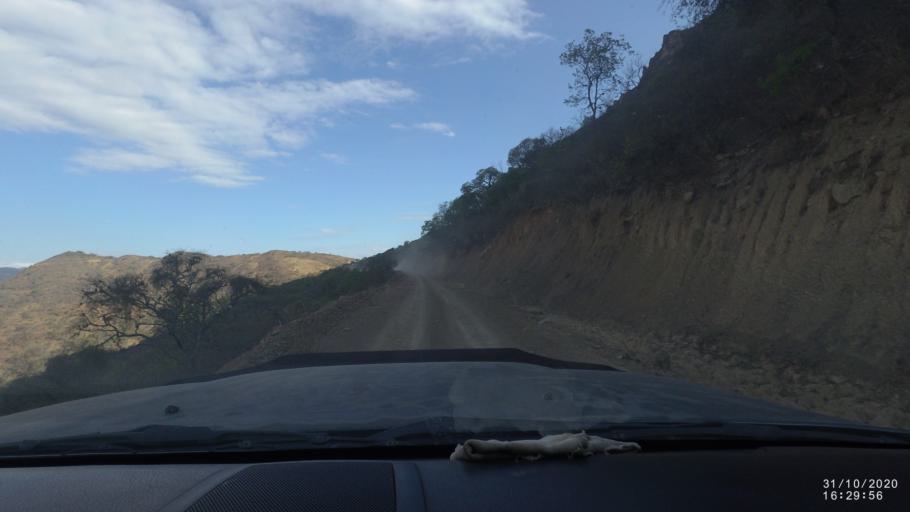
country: BO
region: Chuquisaca
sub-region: Provincia Zudanez
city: Mojocoya
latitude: -18.4234
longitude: -64.5844
